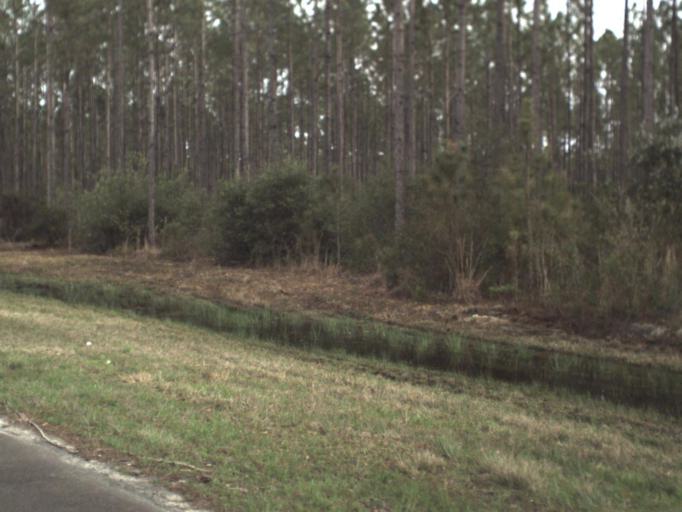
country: US
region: Florida
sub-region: Gulf County
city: Wewahitchka
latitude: 30.1334
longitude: -85.3536
